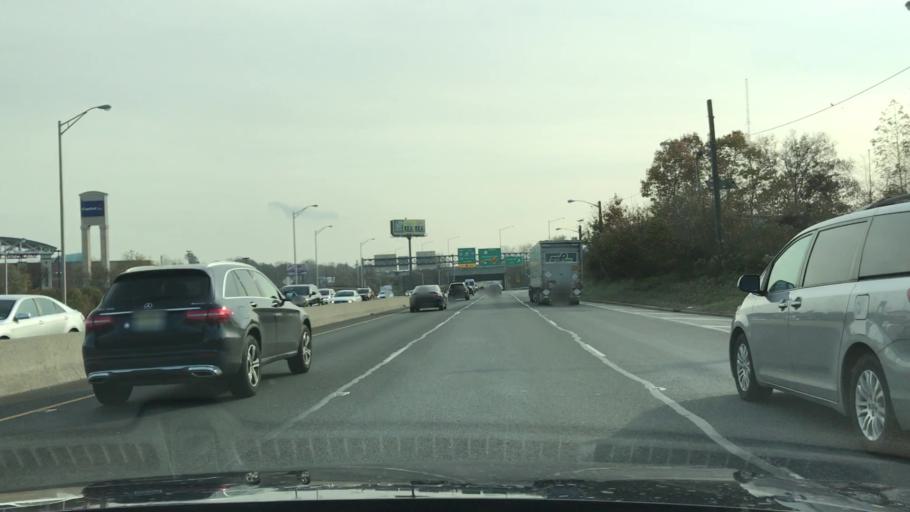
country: US
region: New Jersey
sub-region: Bergen County
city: Lodi
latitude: 40.8890
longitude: -74.0697
